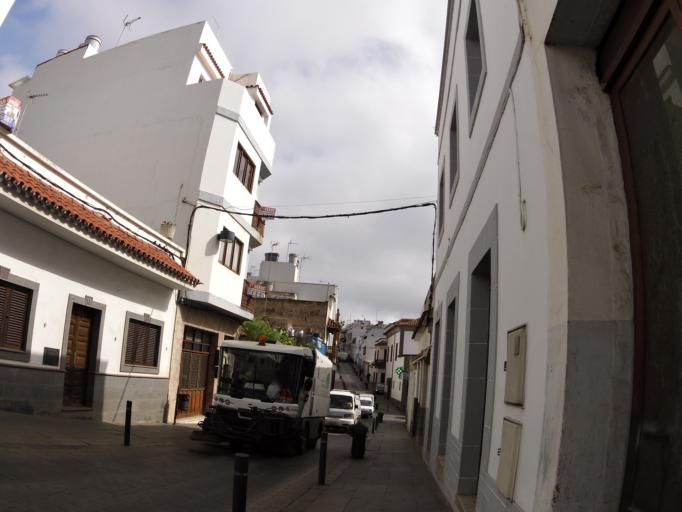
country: ES
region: Canary Islands
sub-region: Provincia de Las Palmas
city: Teror
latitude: 28.0596
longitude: -15.5487
